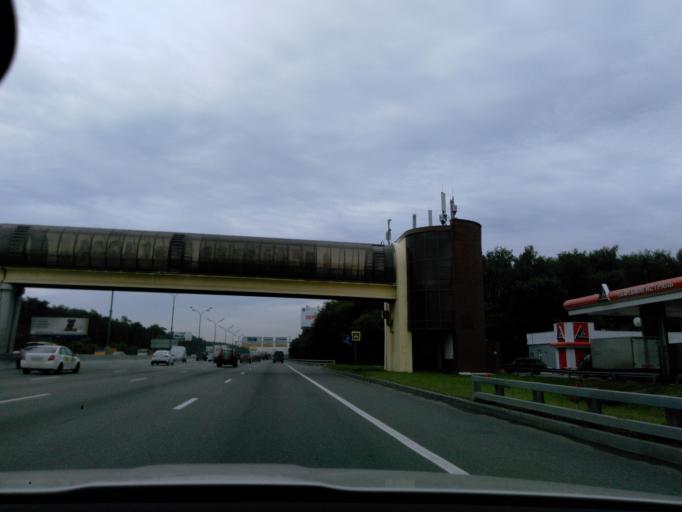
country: RU
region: Moskovskaya
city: Kotel'niki
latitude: 55.6684
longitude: 37.8372
